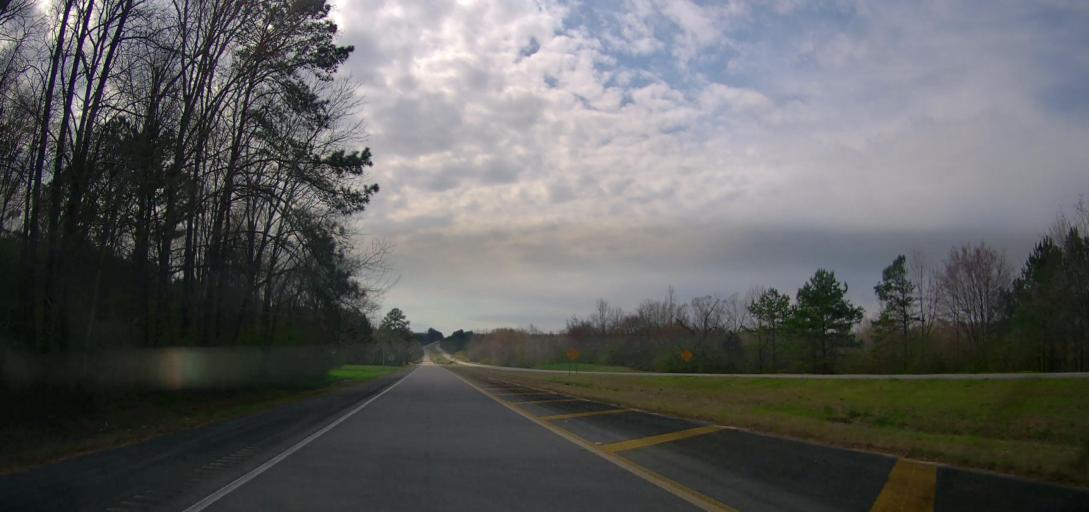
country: US
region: Alabama
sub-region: Marion County
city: Winfield
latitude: 33.9294
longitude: -87.6753
